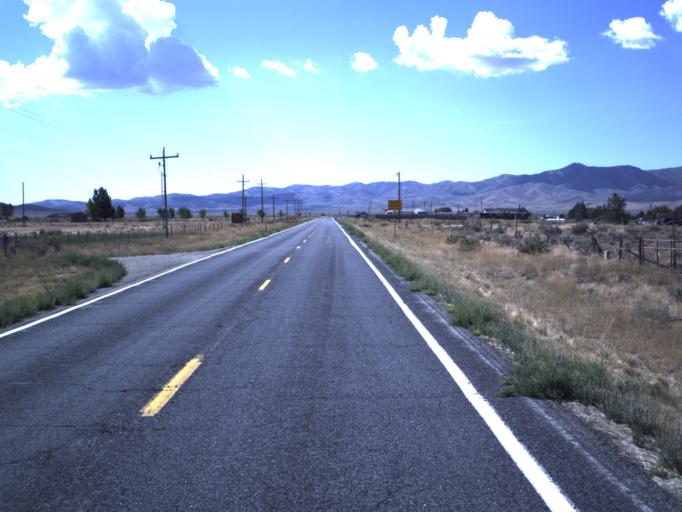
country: US
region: Utah
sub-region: Tooele County
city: Tooele
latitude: 40.0965
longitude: -112.4309
